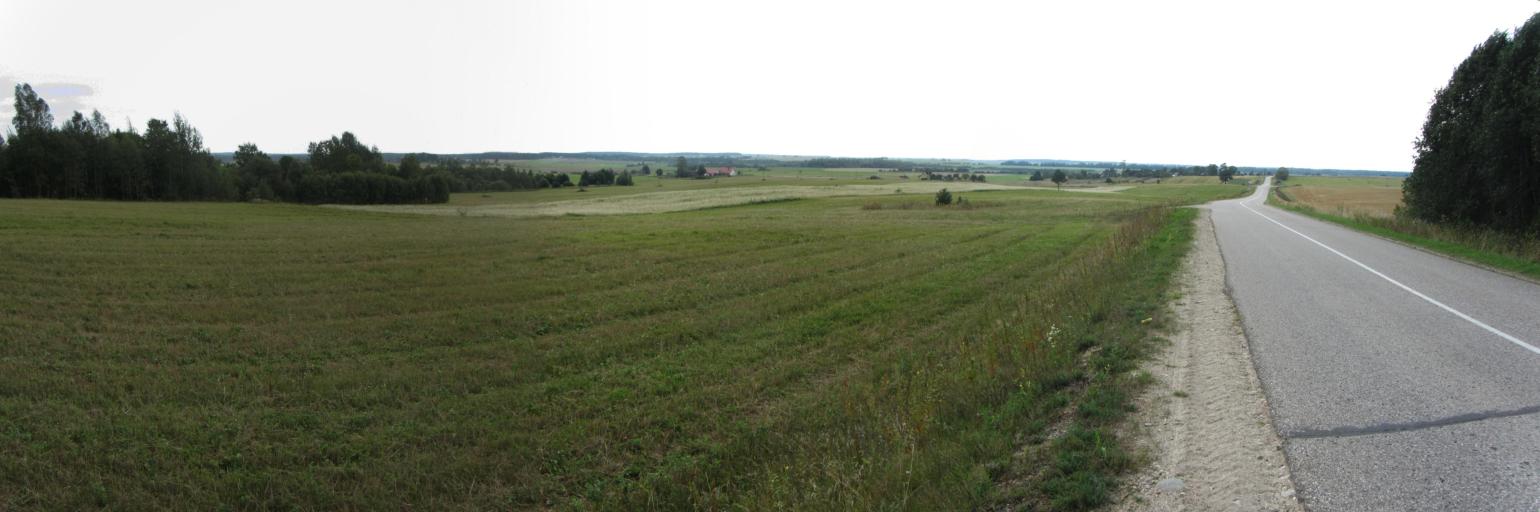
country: LT
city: Salcininkai
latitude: 54.3578
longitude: 25.4773
